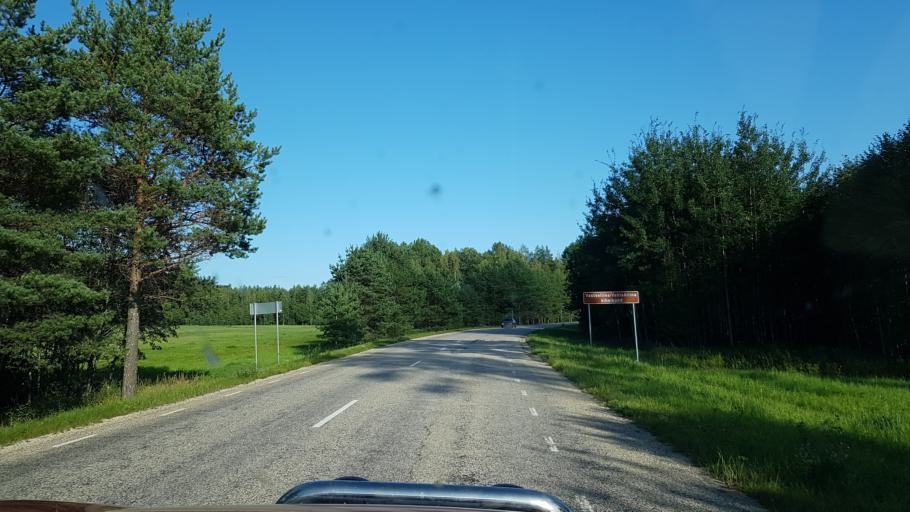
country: EE
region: Vorumaa
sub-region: Voru linn
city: Voru
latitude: 57.8289
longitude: 27.2656
